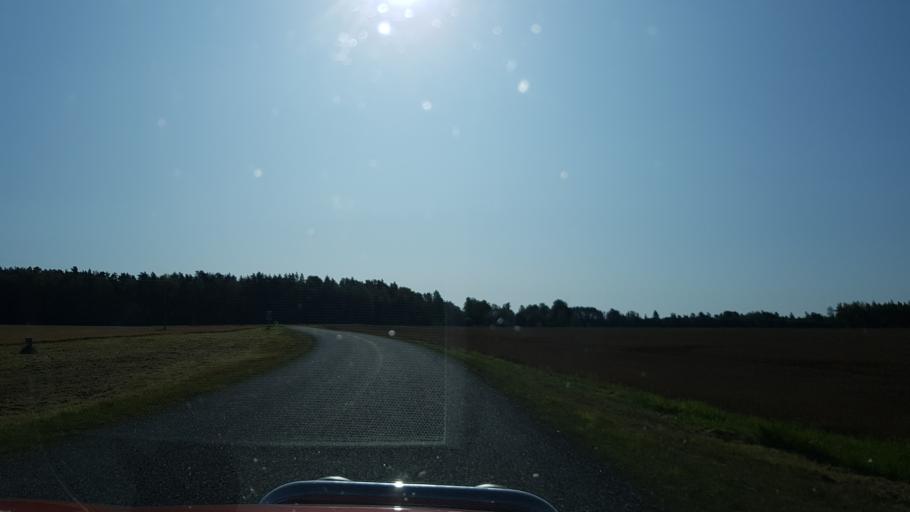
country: LV
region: Apes Novads
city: Ape
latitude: 57.6594
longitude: 26.7043
